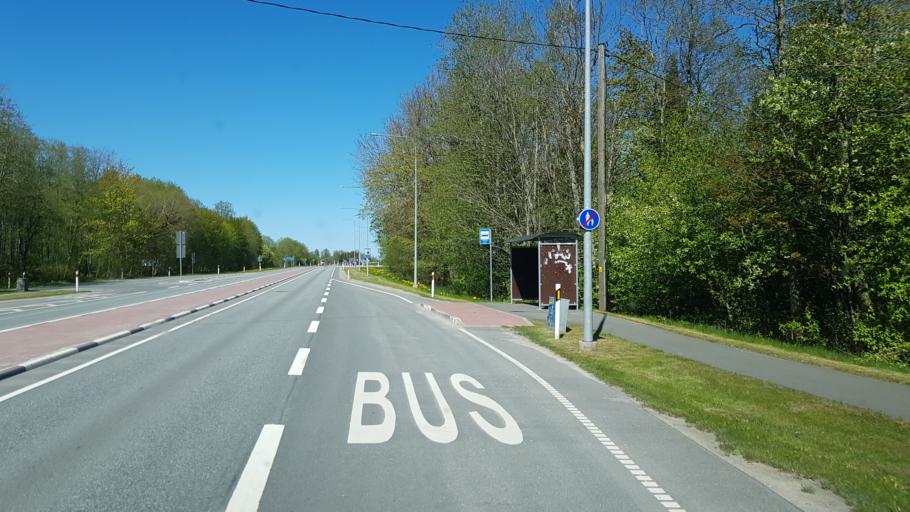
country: EE
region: Viljandimaa
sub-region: Vohma linn
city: Vohma
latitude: 58.6297
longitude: 25.5712
